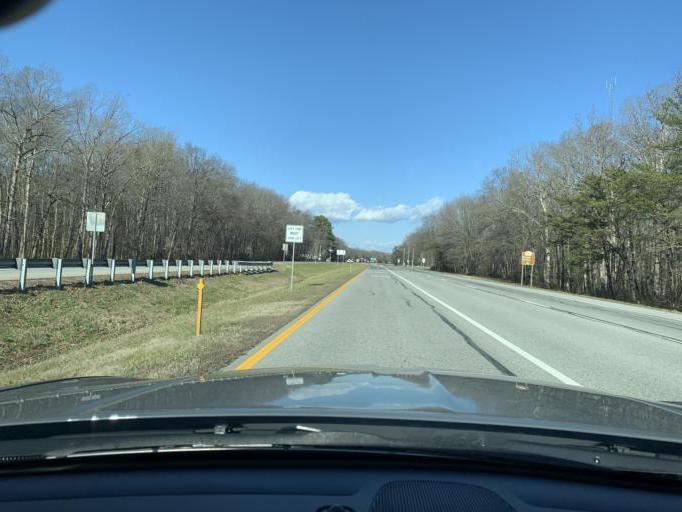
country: US
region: Delaware
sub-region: New Castle County
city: Townsend
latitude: 39.3173
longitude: -75.8472
